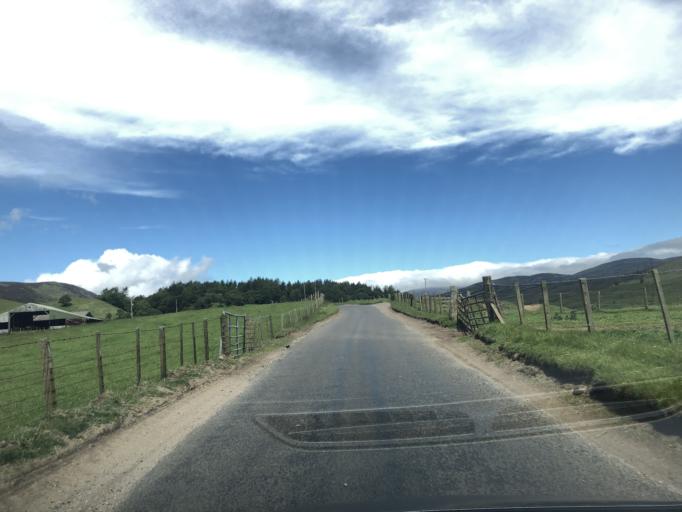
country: GB
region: Scotland
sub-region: Angus
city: Kirriemuir
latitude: 56.7596
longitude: -3.0187
